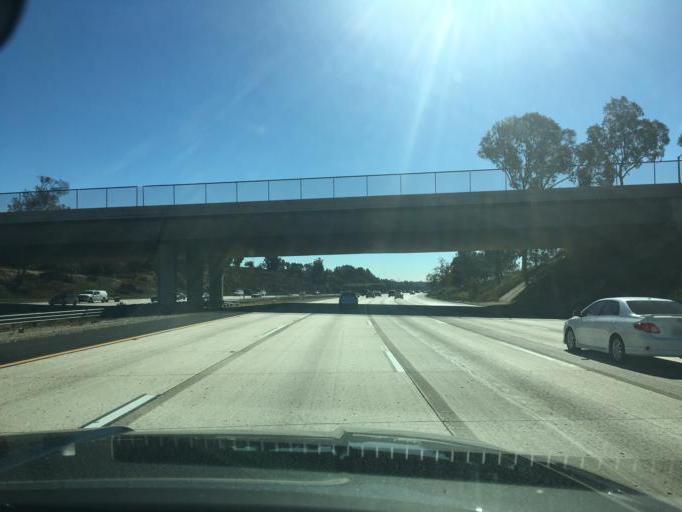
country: US
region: California
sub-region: San Diego County
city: La Mesa
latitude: 32.8345
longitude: -117.1195
